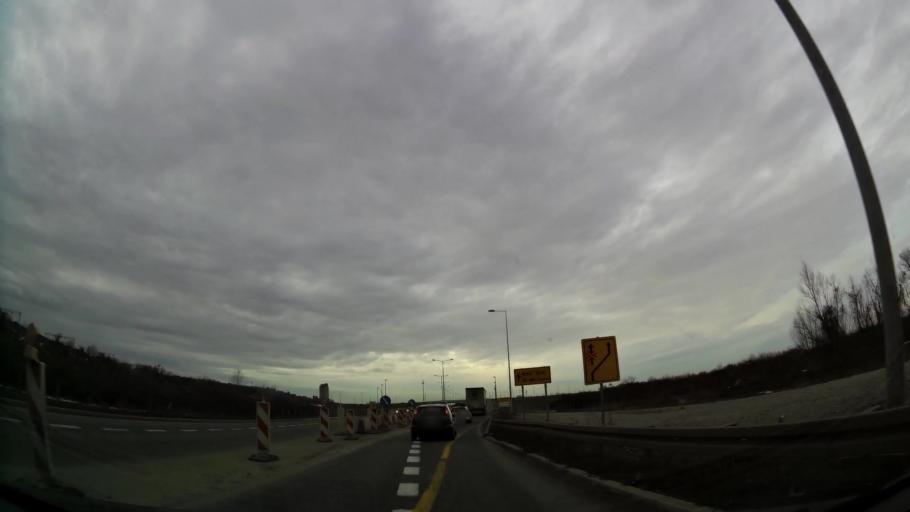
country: RS
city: Ostruznica
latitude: 44.7310
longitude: 20.3402
